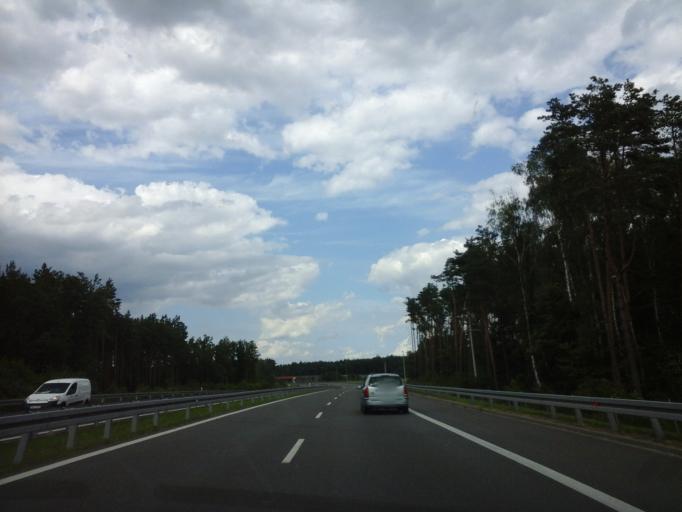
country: PL
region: West Pomeranian Voivodeship
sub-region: Powiat goleniowski
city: Goleniow
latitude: 53.6182
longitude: 14.8179
